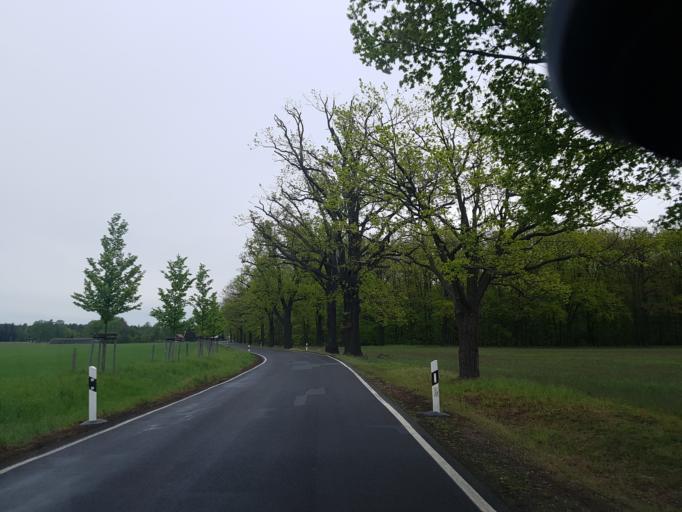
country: DE
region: Brandenburg
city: Spremberg
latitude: 51.6399
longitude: 14.4334
